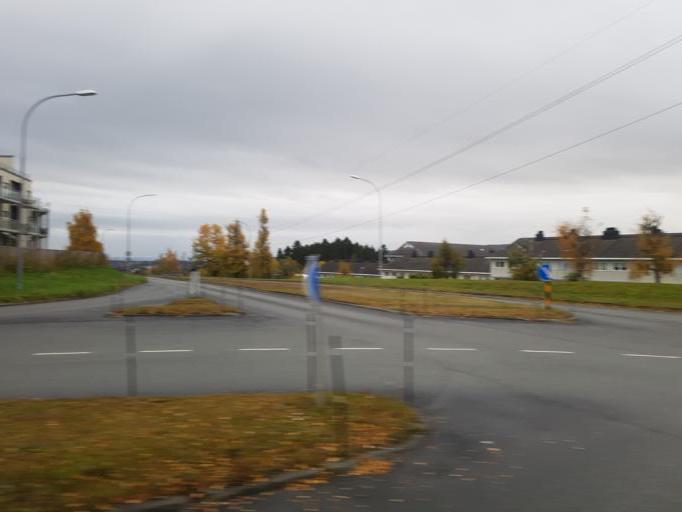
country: NO
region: Sor-Trondelag
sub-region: Trondheim
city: Trondheim
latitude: 63.3726
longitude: 10.3474
